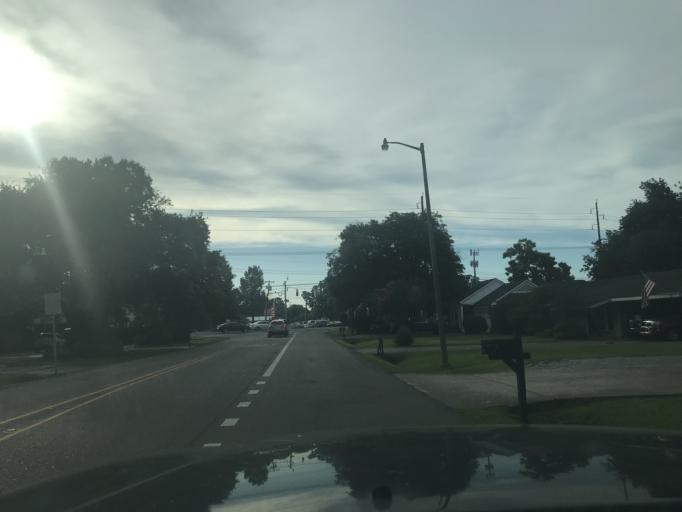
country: US
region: Louisiana
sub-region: Lafayette Parish
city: Lafayette
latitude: 30.1958
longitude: -92.0563
